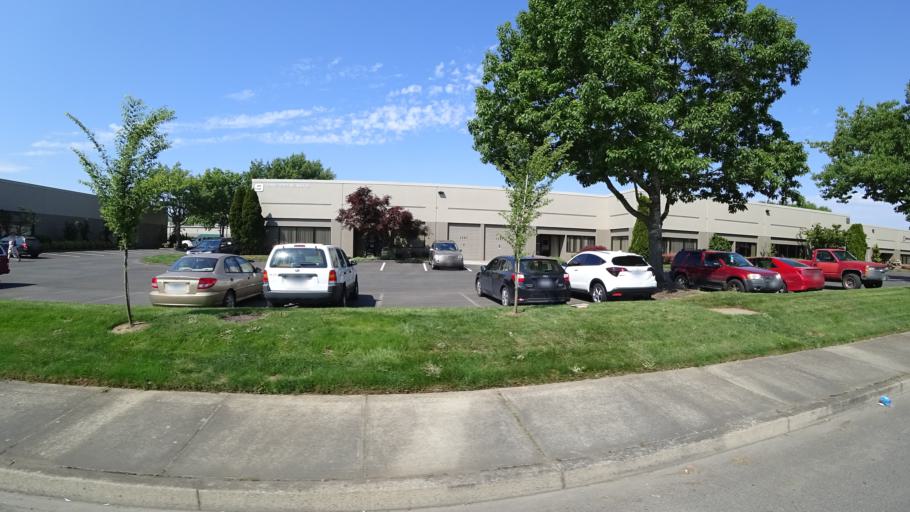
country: US
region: Oregon
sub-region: Multnomah County
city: Lents
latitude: 45.5592
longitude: -122.5358
